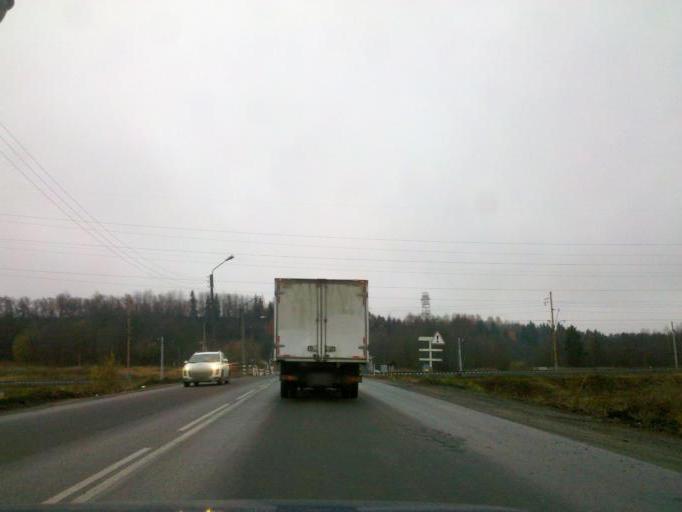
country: RU
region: Republic of Karelia
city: Petrozavodsk
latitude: 61.8221
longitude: 34.2627
